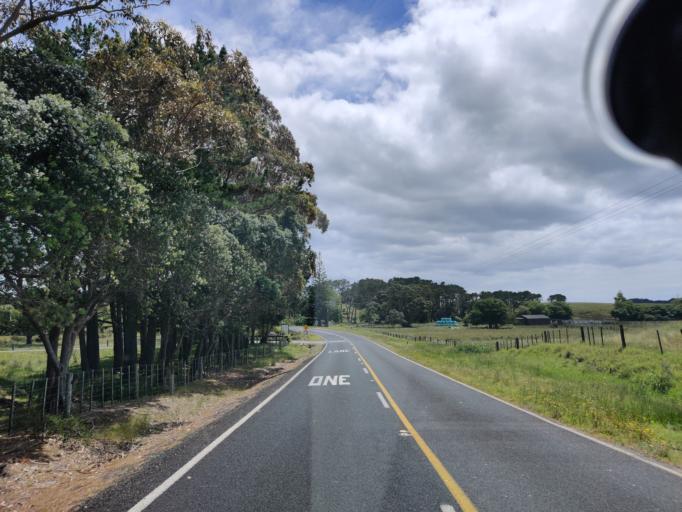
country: NZ
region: Northland
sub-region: Far North District
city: Kaitaia
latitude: -34.7097
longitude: 173.0348
